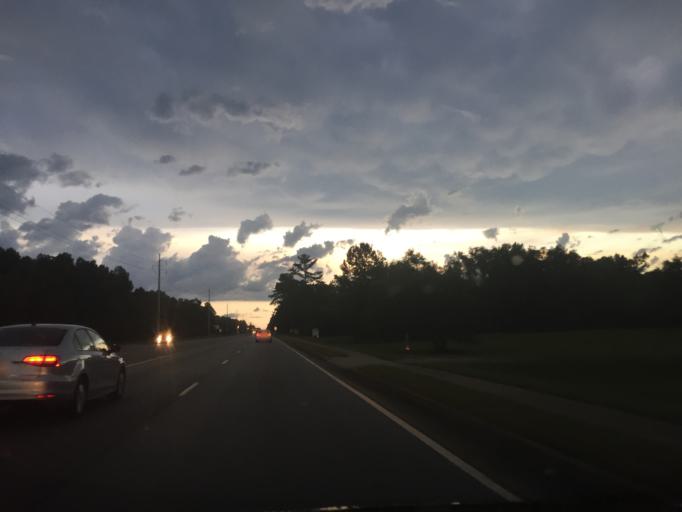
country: US
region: Georgia
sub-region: Liberty County
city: Hinesville
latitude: 31.8564
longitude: -81.5599
